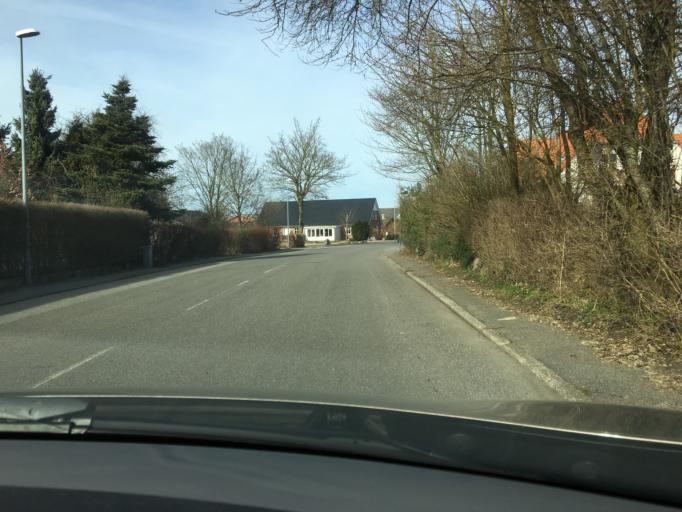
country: DK
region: Central Jutland
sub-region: Hedensted Kommune
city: Hedensted
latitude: 55.7338
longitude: 9.6614
